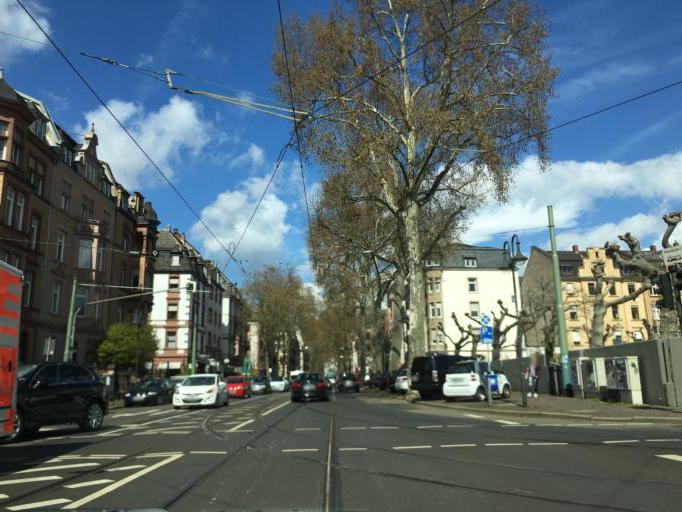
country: DE
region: Hesse
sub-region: Regierungsbezirk Darmstadt
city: Frankfurt am Main
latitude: 50.0988
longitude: 8.6831
